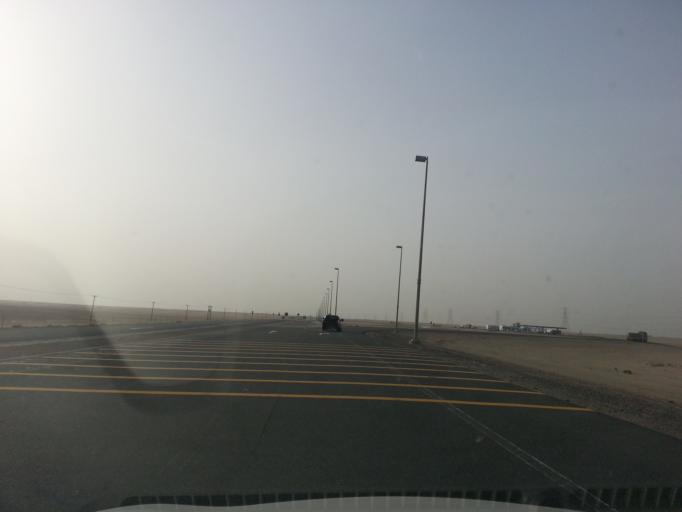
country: AE
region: Dubai
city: Dubai
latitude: 24.8011
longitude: 55.0711
